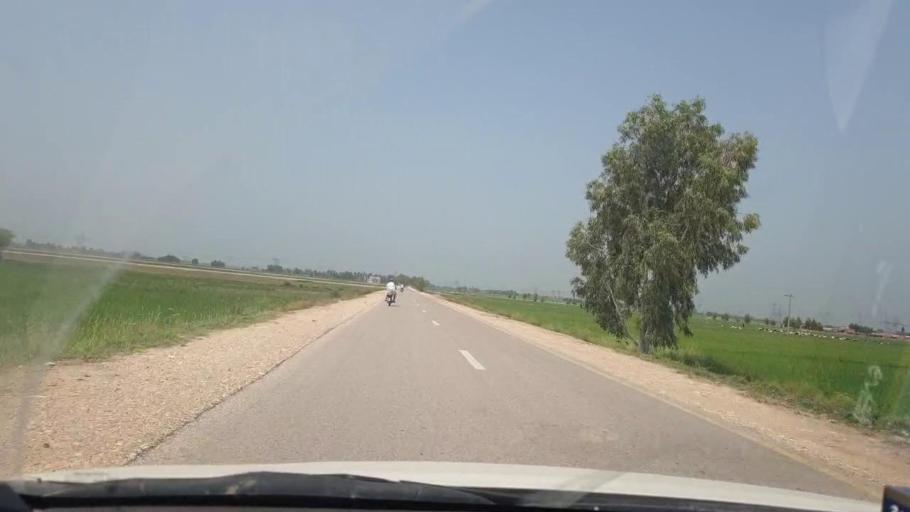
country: PK
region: Sindh
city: Rustam jo Goth
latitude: 27.9592
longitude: 68.7545
